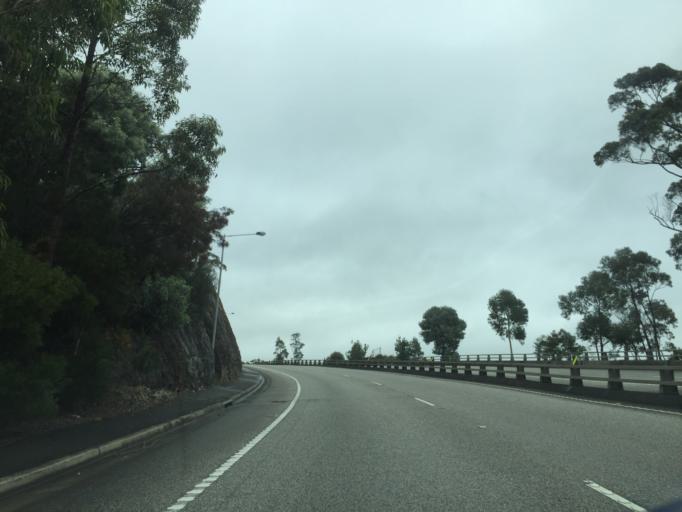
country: AU
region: New South Wales
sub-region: Blue Mountains Municipality
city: Hazelbrook
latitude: -33.7149
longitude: 150.5115
